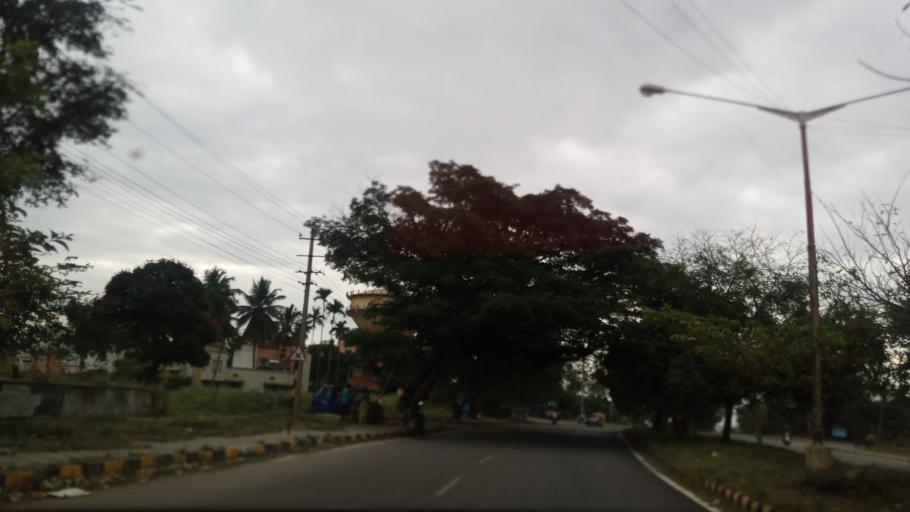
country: IN
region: Karnataka
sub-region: Mysore
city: Mysore
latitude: 12.2905
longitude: 76.6229
